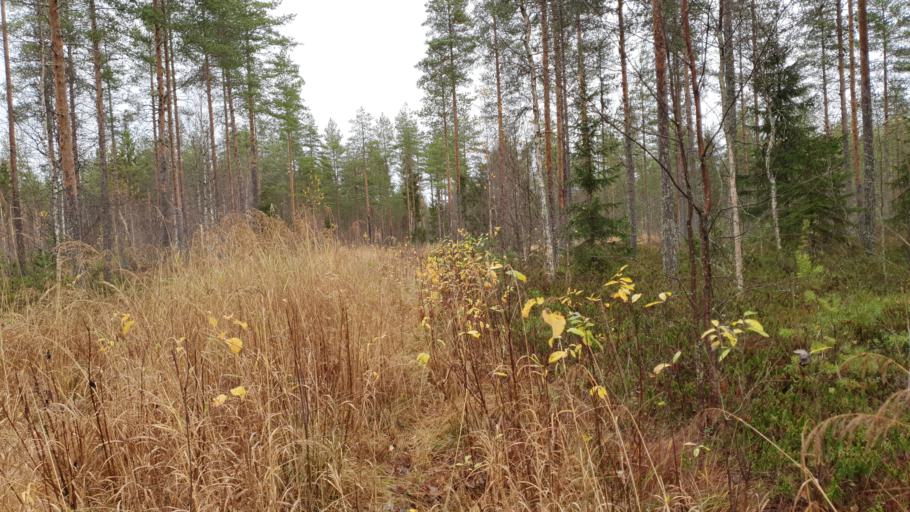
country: FI
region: Kainuu
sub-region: Kehys-Kainuu
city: Kuhmo
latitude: 64.1422
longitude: 29.4191
